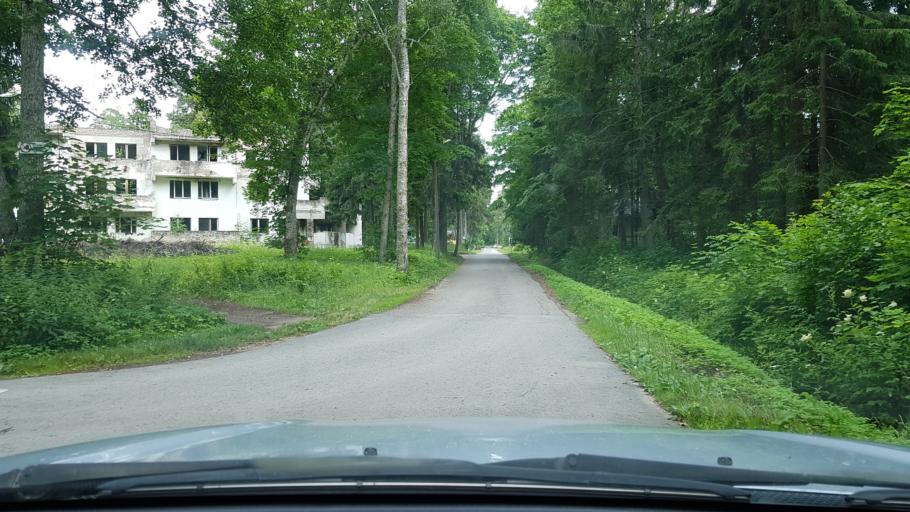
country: EE
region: Ida-Virumaa
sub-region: Narva-Joesuu linn
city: Narva-Joesuu
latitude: 59.4513
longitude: 28.0240
